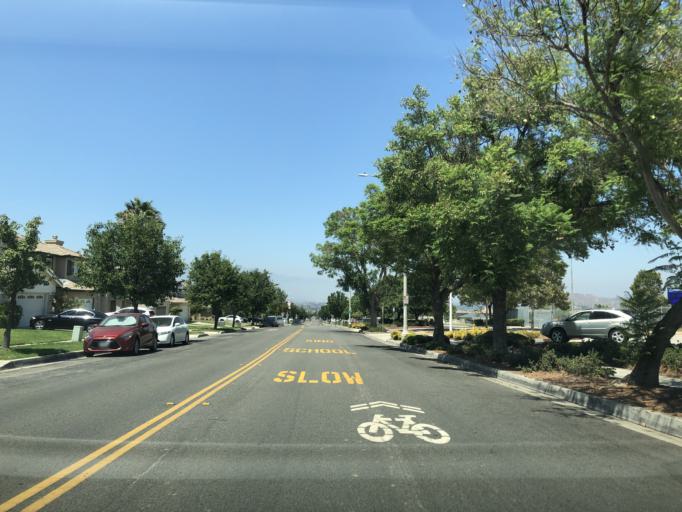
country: US
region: California
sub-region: Riverside County
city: Corona
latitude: 33.8512
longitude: -117.5815
